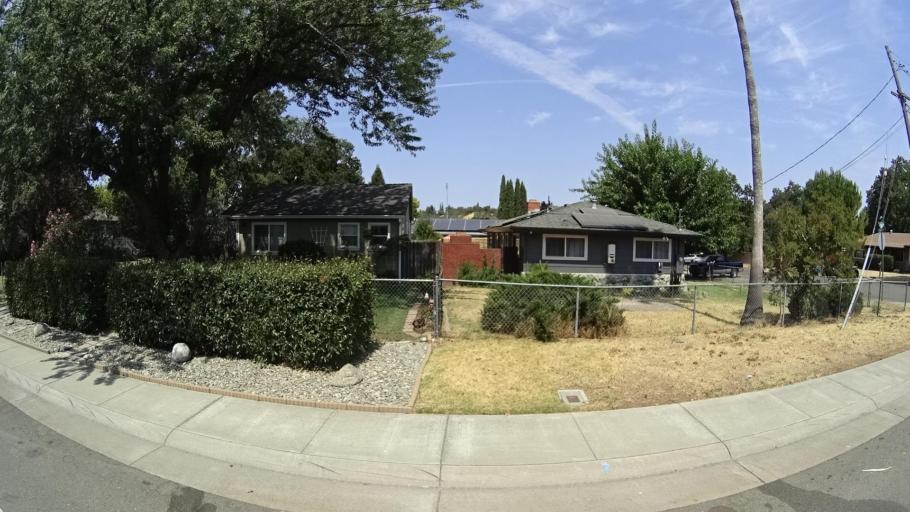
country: US
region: California
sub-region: Placer County
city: Rocklin
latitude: 38.7950
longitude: -121.2375
